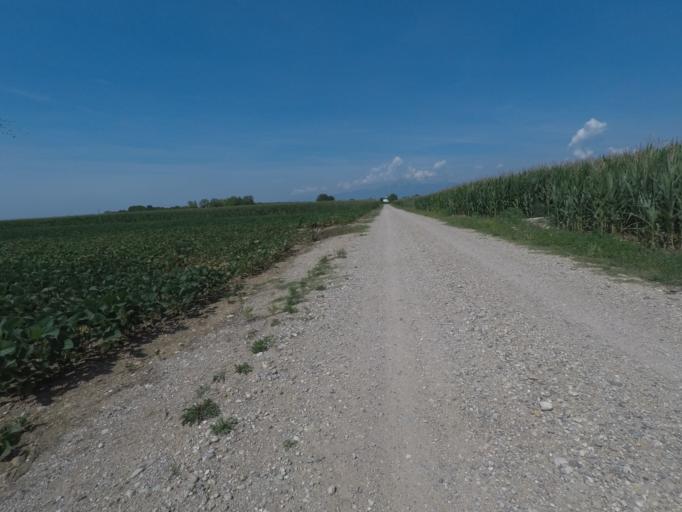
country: IT
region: Friuli Venezia Giulia
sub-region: Provincia di Udine
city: Dignano
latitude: 46.0837
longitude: 12.9526
